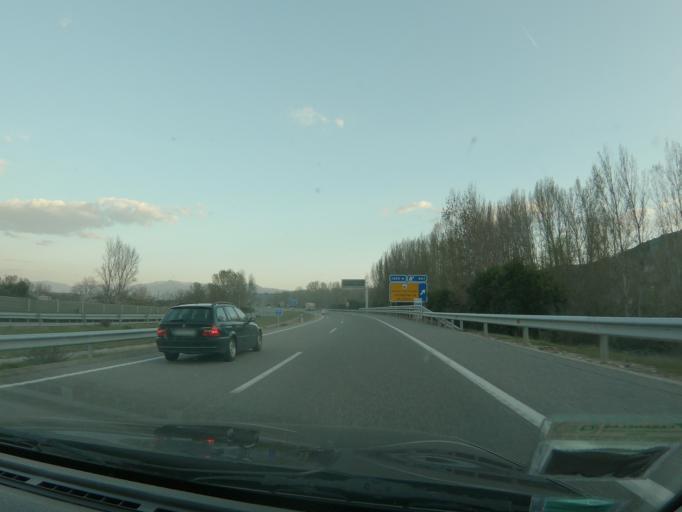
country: ES
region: Castille and Leon
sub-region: Provincia de Leon
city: Villafranca del Bierzo
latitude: 42.6017
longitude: -6.8174
